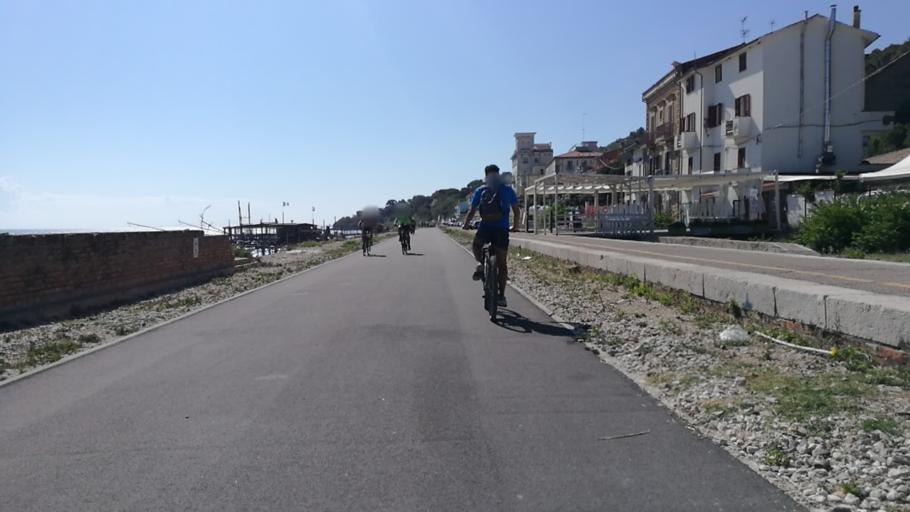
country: IT
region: Abruzzo
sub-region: Provincia di Chieti
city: Marina di San Vito
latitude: 42.3067
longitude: 14.4493
